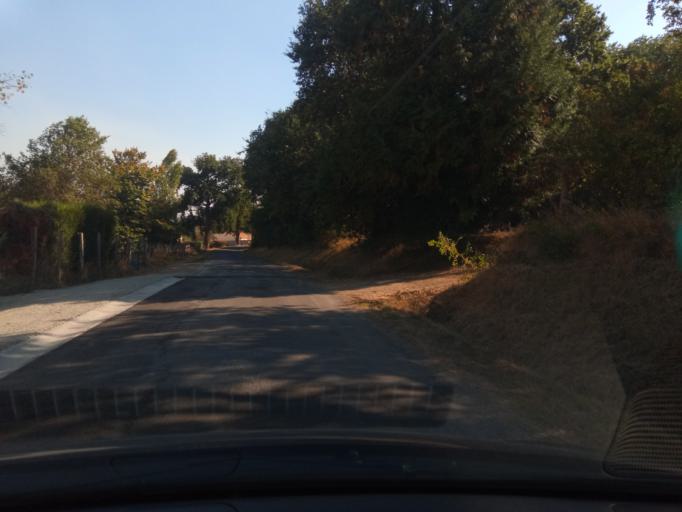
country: FR
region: Poitou-Charentes
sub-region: Departement de la Vienne
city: Montmorillon
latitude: 46.4134
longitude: 0.8757
